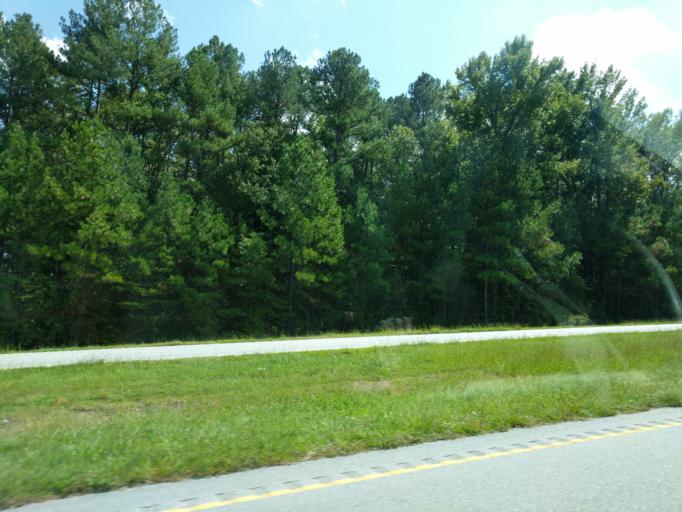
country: US
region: South Carolina
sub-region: Spartanburg County
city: Woodruff
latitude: 34.8106
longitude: -82.0037
